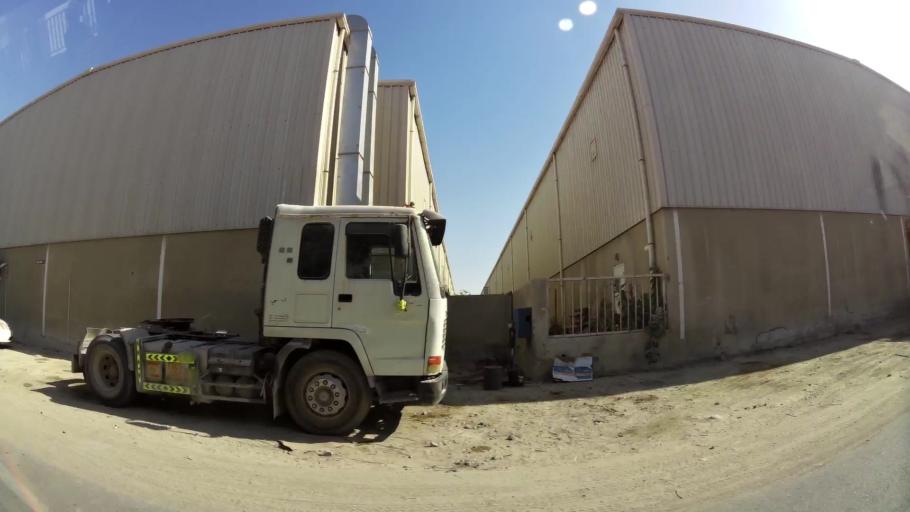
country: AE
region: Dubai
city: Dubai
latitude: 24.9882
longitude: 55.0995
